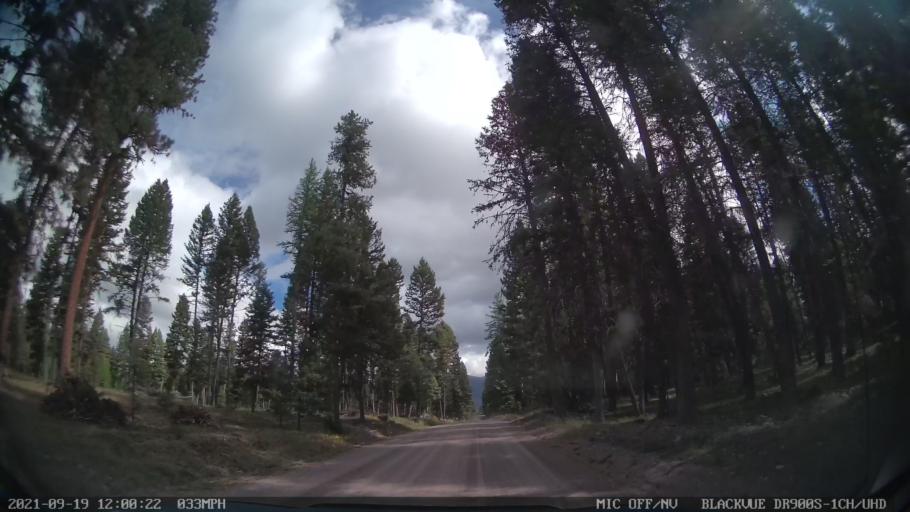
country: US
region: Montana
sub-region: Missoula County
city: Seeley Lake
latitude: 47.1885
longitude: -113.4668
